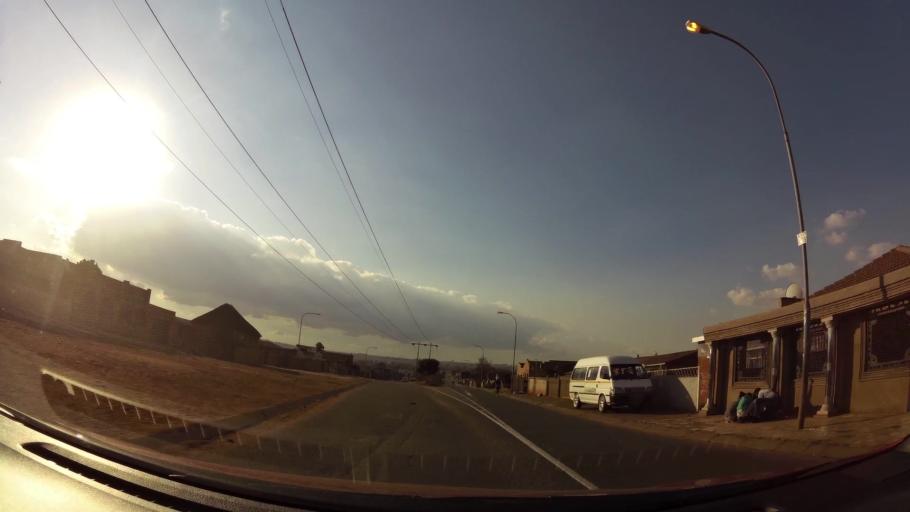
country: ZA
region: Gauteng
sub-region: City of Johannesburg Metropolitan Municipality
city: Soweto
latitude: -26.2278
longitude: 27.8584
